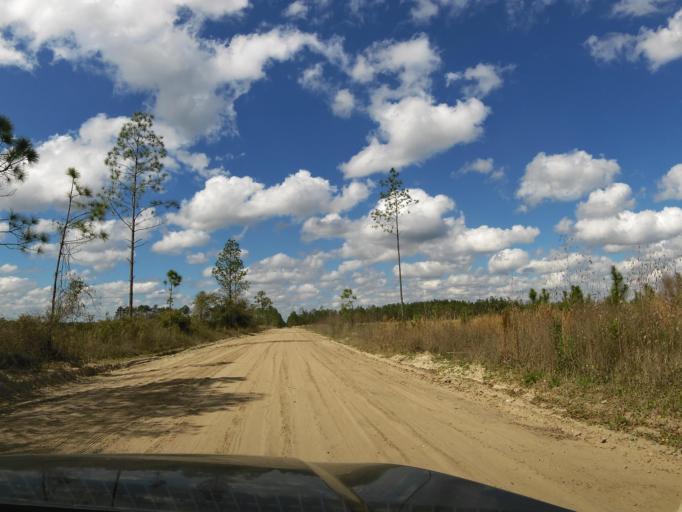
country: US
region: Florida
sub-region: Clay County
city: Green Cove Springs
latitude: 29.8375
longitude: -81.7273
